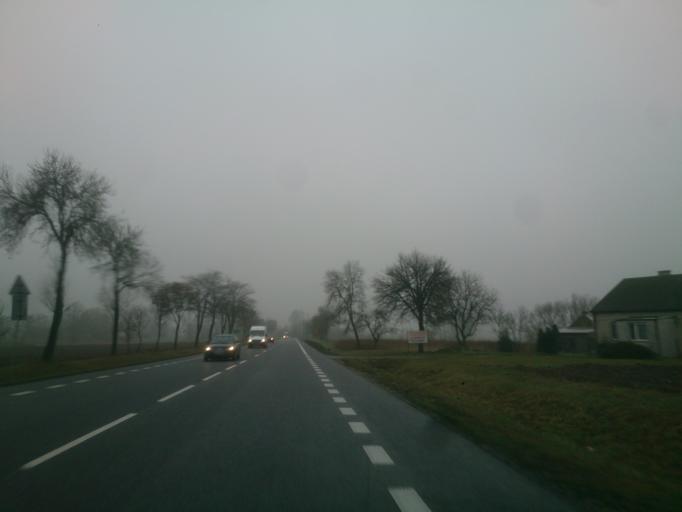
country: PL
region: Masovian Voivodeship
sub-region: Powiat sierpecki
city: Rosciszewo
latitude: 52.8205
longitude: 19.7782
